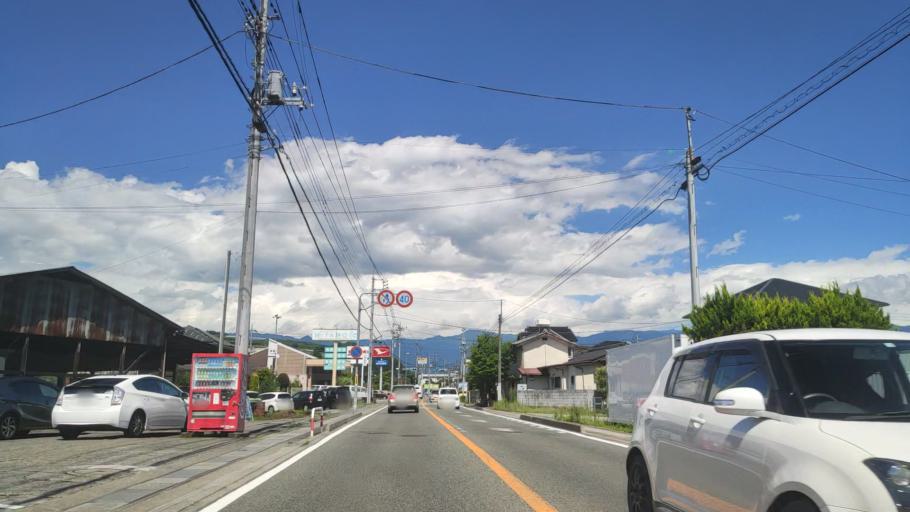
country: JP
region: Yamanashi
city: Isawa
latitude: 35.6865
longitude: 138.6689
